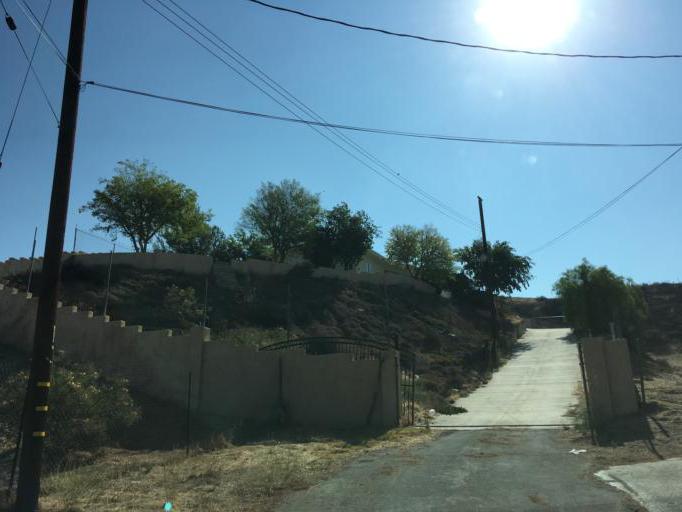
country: US
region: California
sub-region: Los Angeles County
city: Val Verde
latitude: 34.4527
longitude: -118.6593
